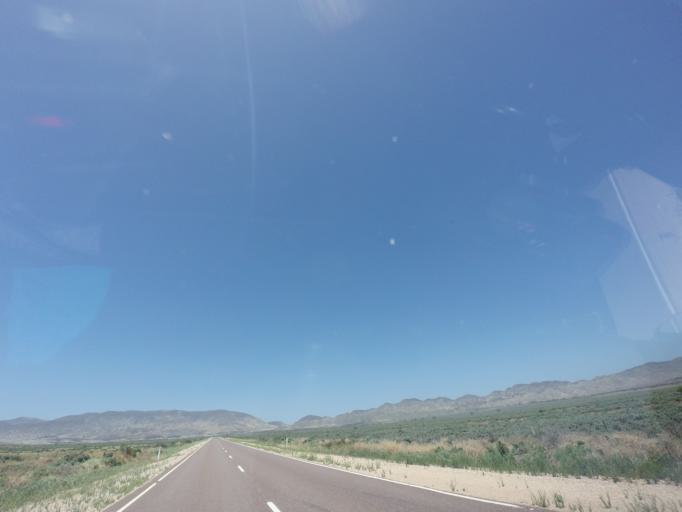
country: AU
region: South Australia
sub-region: Port Augusta
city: Port Augusta
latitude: -32.6235
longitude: 137.9549
